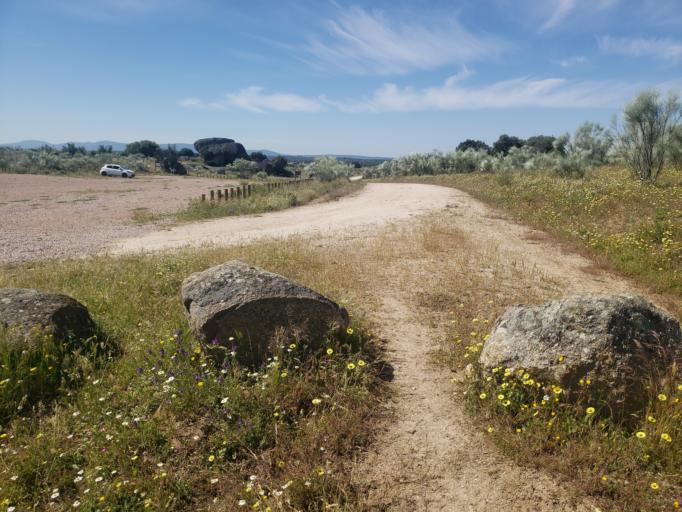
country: ES
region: Extremadura
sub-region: Provincia de Caceres
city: Malpartida de Caceres
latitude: 39.4200
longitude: -6.4997
